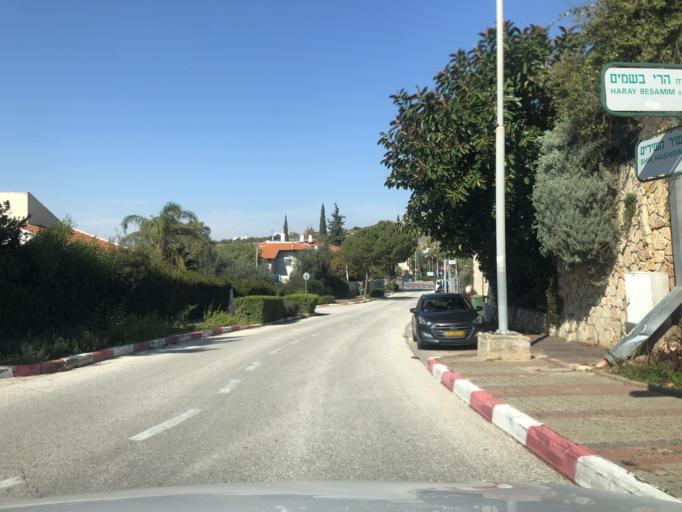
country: PS
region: West Bank
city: Azun Atme
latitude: 32.1120
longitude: 35.0318
